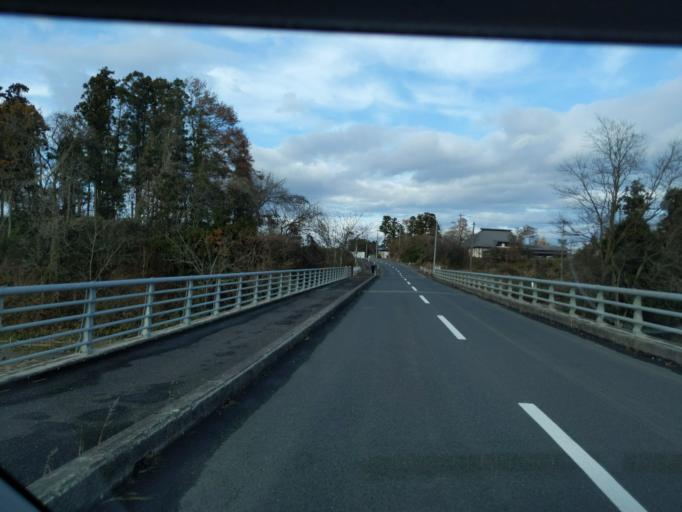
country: JP
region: Iwate
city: Mizusawa
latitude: 39.1835
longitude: 141.1053
